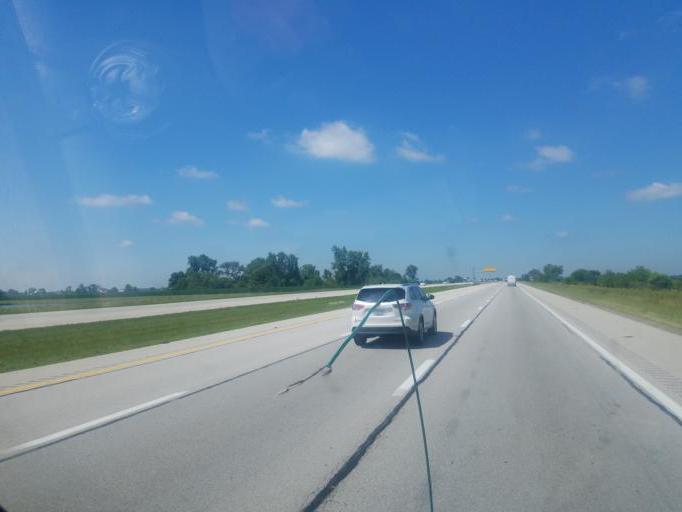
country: US
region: Ohio
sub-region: Greene County
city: Jamestown
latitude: 39.5901
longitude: -83.6637
